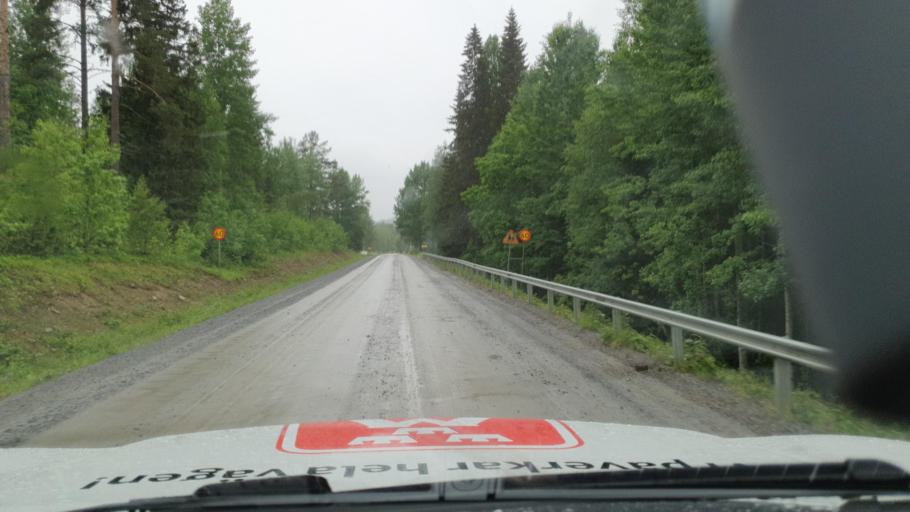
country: SE
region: Vaesterbotten
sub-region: Bjurholms Kommun
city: Bjurholm
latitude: 63.9005
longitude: 19.4040
